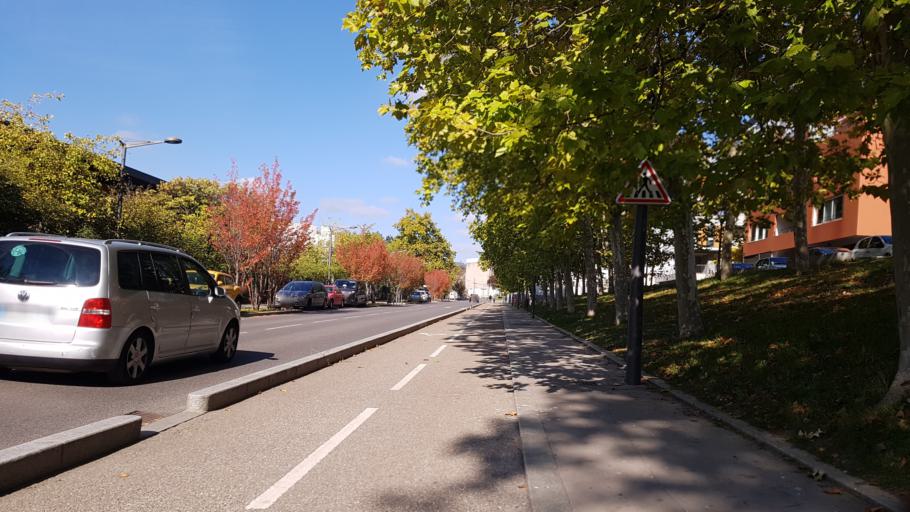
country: FR
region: Rhone-Alpes
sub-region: Departement du Rhone
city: Ecully
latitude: 45.7871
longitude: 4.7931
